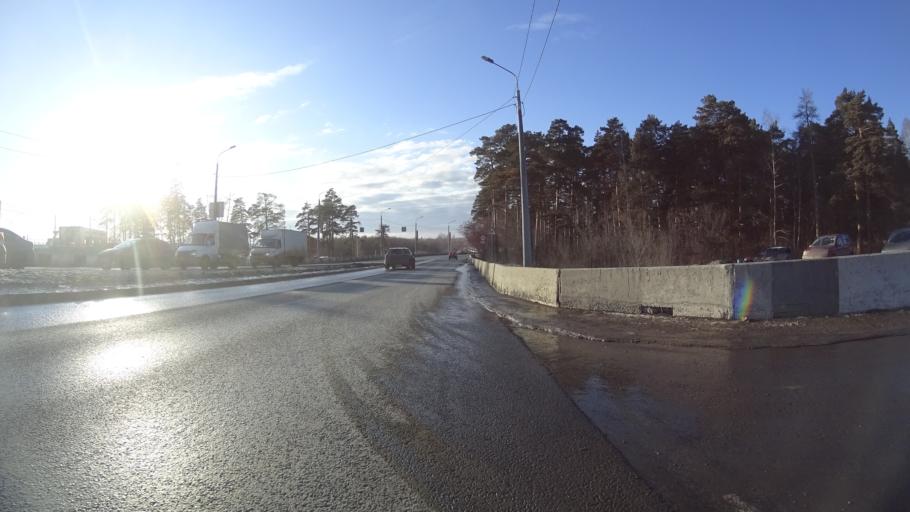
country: RU
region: Chelyabinsk
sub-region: Gorod Chelyabinsk
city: Chelyabinsk
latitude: 55.1475
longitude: 61.3289
